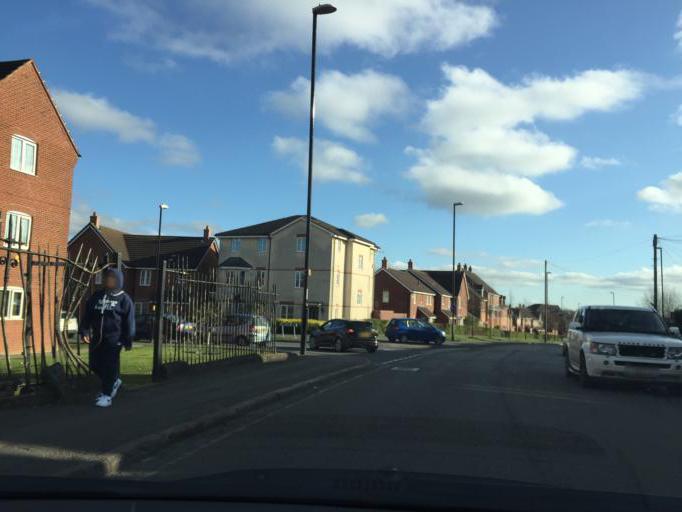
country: GB
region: England
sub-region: Coventry
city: Coventry
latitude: 52.4027
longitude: -1.4867
